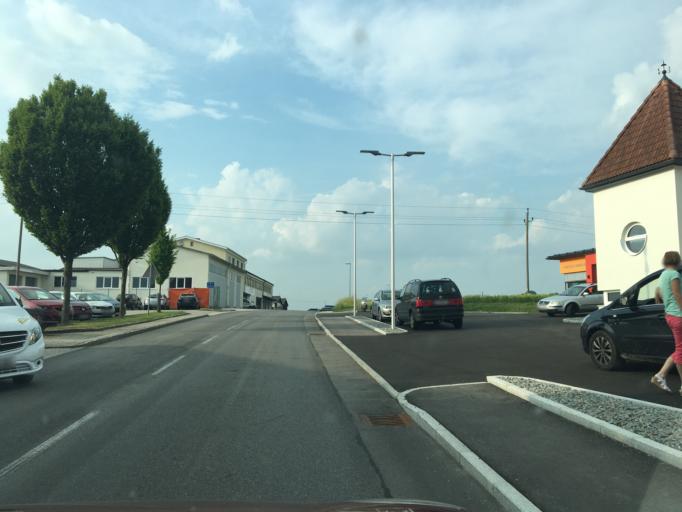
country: AT
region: Upper Austria
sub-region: Politischer Bezirk Vocklabruck
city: Redleiten
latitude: 48.1572
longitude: 13.5628
